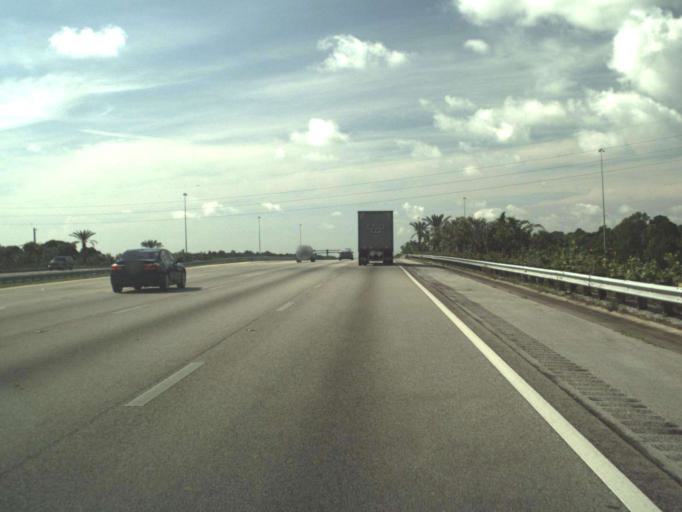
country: US
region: Florida
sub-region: Palm Beach County
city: Limestone Creek
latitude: 26.8847
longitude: -80.1297
